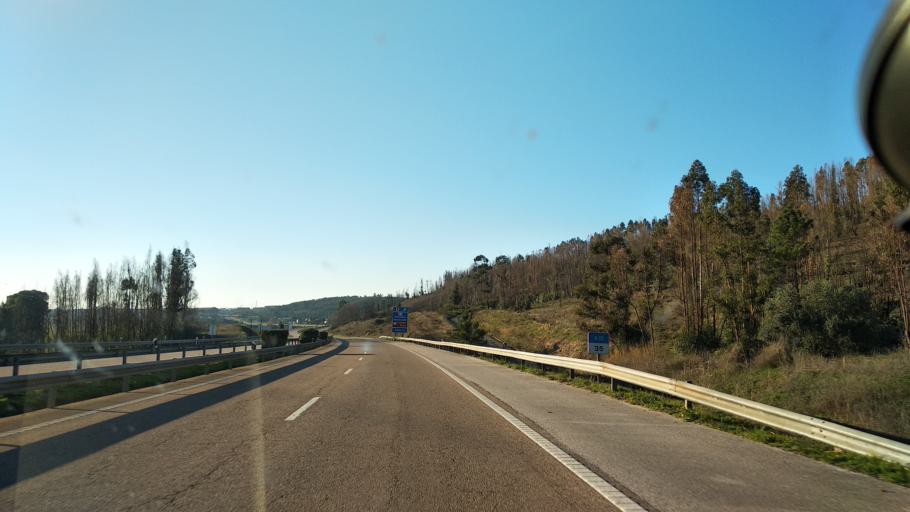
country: PT
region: Santarem
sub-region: Abrantes
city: Tramagal
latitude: 39.4844
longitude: -8.2500
